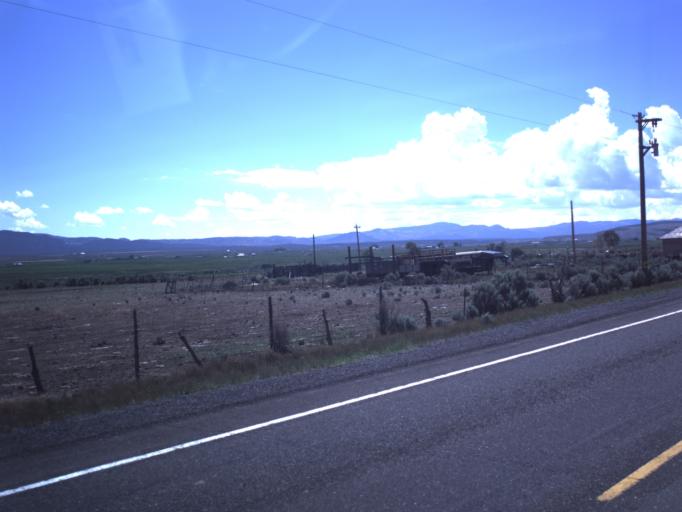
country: US
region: Utah
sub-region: Garfield County
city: Panguitch
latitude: 37.8774
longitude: -112.4368
